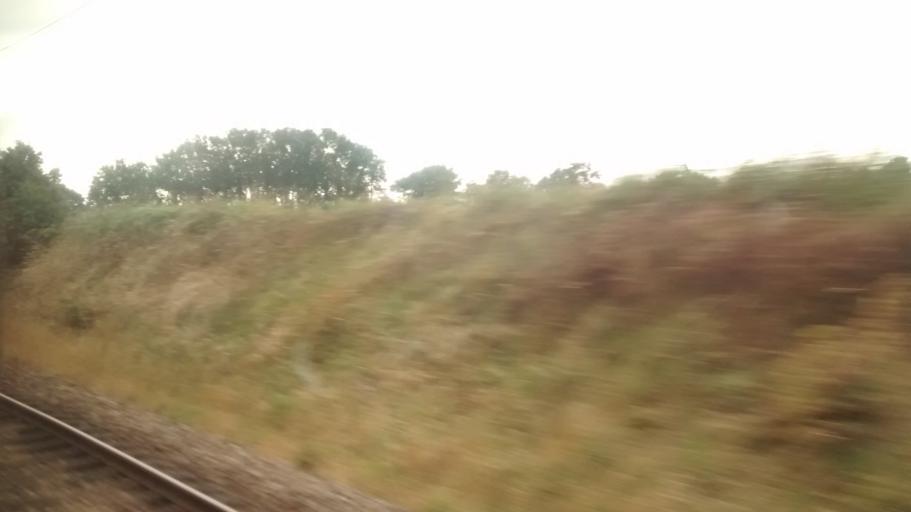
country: FR
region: Pays de la Loire
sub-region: Departement de la Mayenne
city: Montsurs
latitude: 48.1499
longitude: -0.5081
